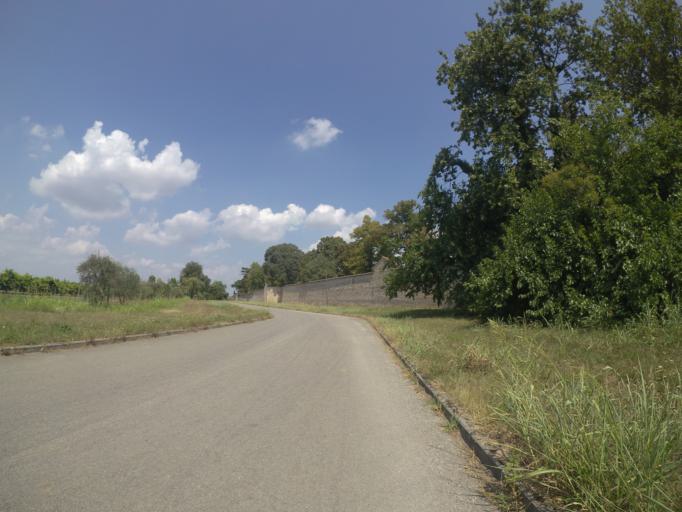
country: IT
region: Friuli Venezia Giulia
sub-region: Provincia di Udine
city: Codroipo
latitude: 45.9510
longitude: 13.0086
